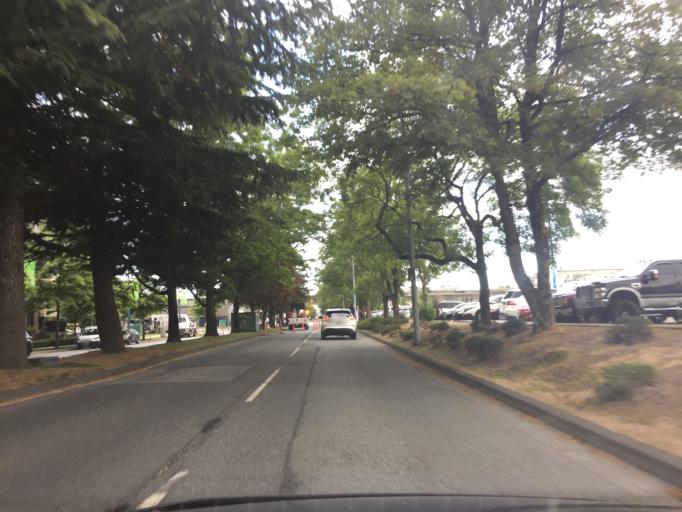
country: CA
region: British Columbia
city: Richmond
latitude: 49.1739
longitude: -123.1337
